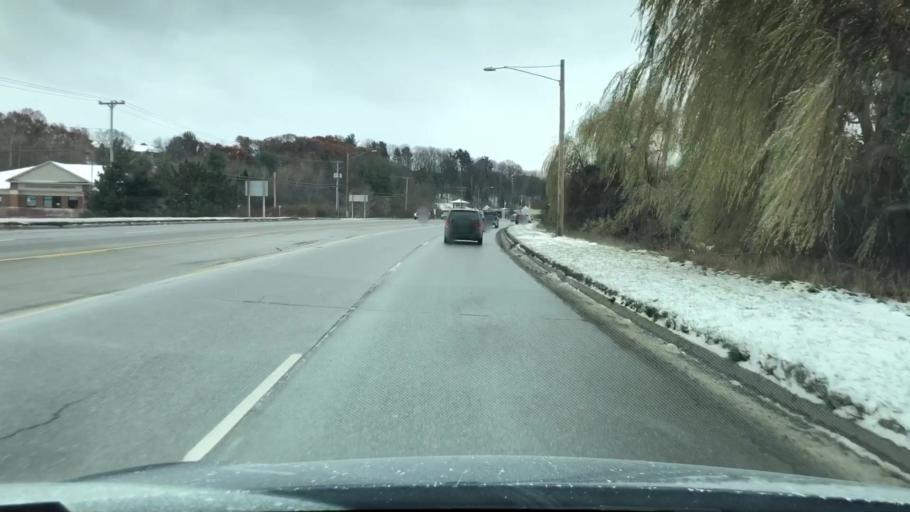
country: US
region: Michigan
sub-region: Grand Traverse County
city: Traverse City
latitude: 44.7506
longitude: -85.6352
